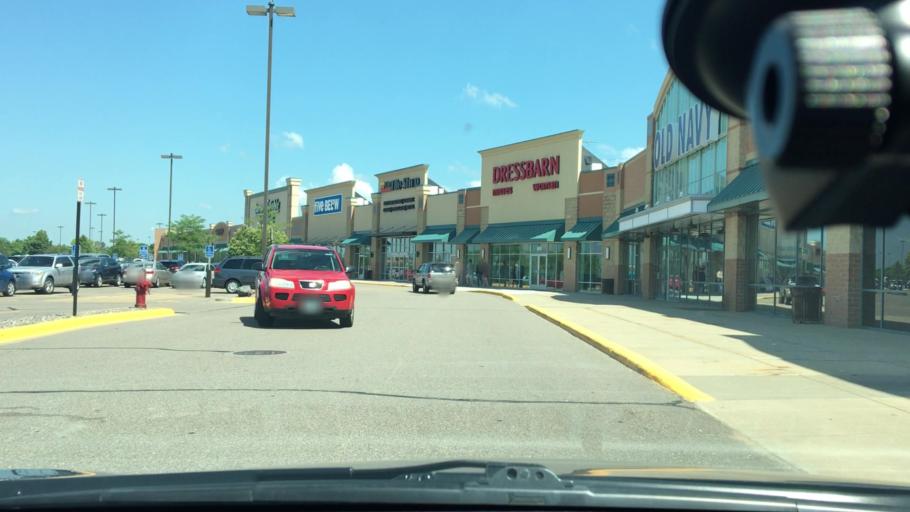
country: US
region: Minnesota
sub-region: Hennepin County
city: Maple Grove
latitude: 45.0992
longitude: -93.4474
